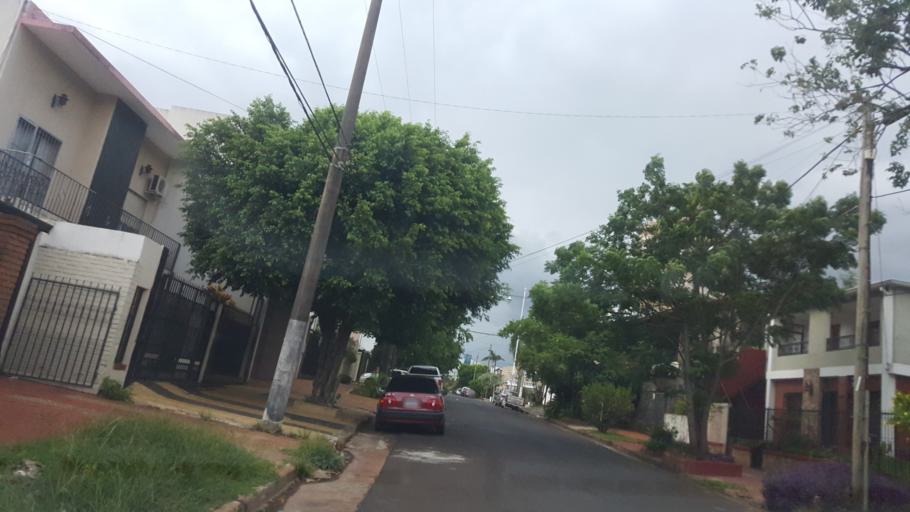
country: AR
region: Misiones
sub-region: Departamento de Capital
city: Posadas
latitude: -27.3598
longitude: -55.8958
